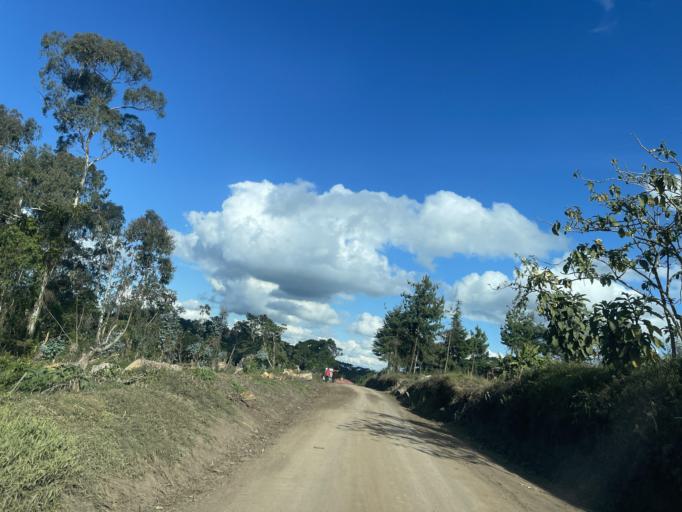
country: TZ
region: Iringa
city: Makungu
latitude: -8.4778
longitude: 35.4201
